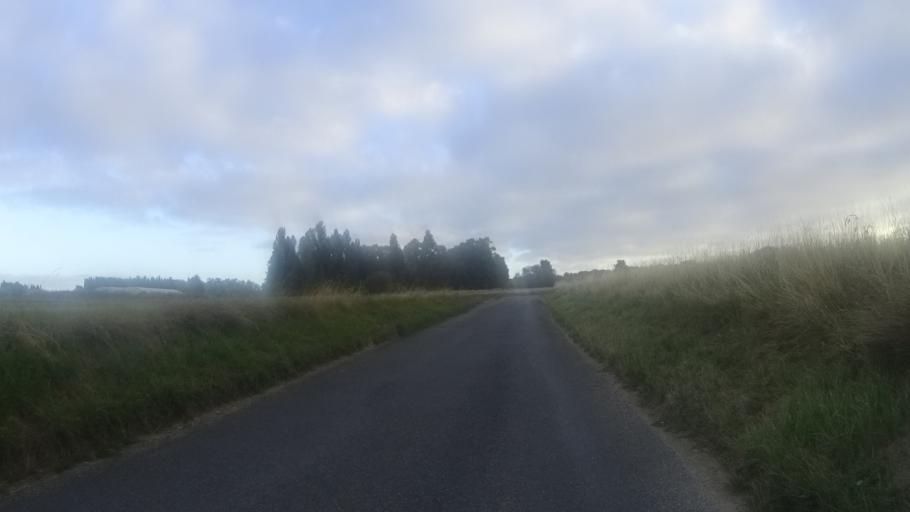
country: FR
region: Ile-de-France
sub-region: Departement de l'Essonne
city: Vert-le-Petit
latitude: 48.5657
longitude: 2.3870
